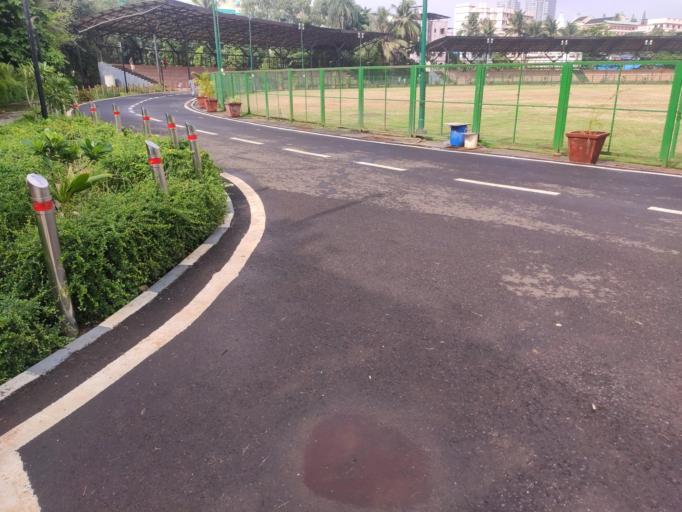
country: IN
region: Maharashtra
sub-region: Mumbai Suburban
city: Borivli
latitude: 19.2456
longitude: 72.8567
